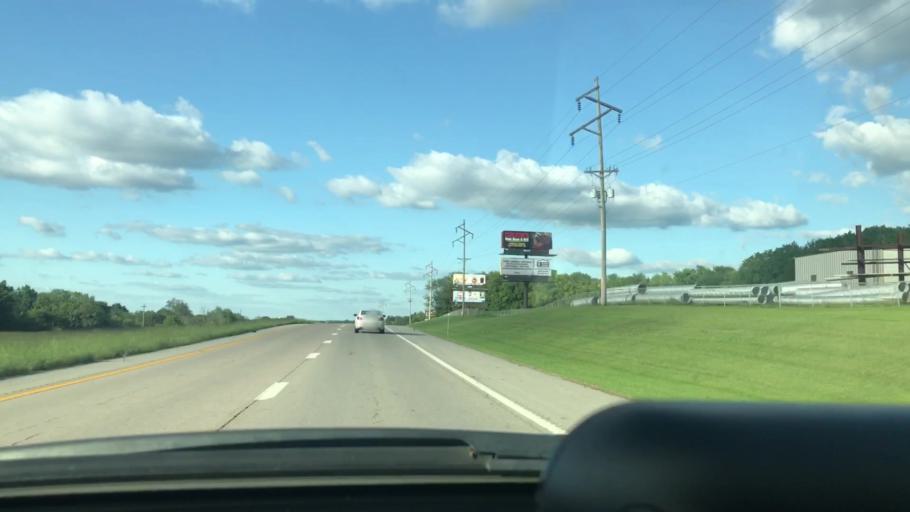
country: US
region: Missouri
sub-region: Pettis County
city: Sedalia
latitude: 38.6413
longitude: -93.2639
